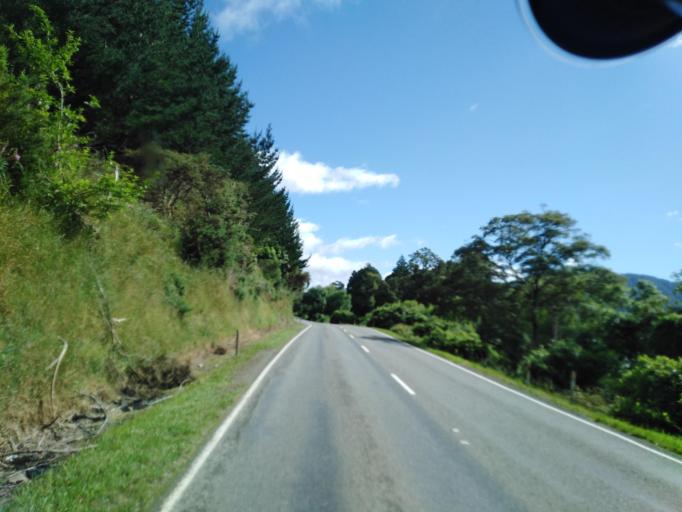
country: NZ
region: Nelson
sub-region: Nelson City
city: Nelson
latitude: -41.2590
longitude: 173.5755
